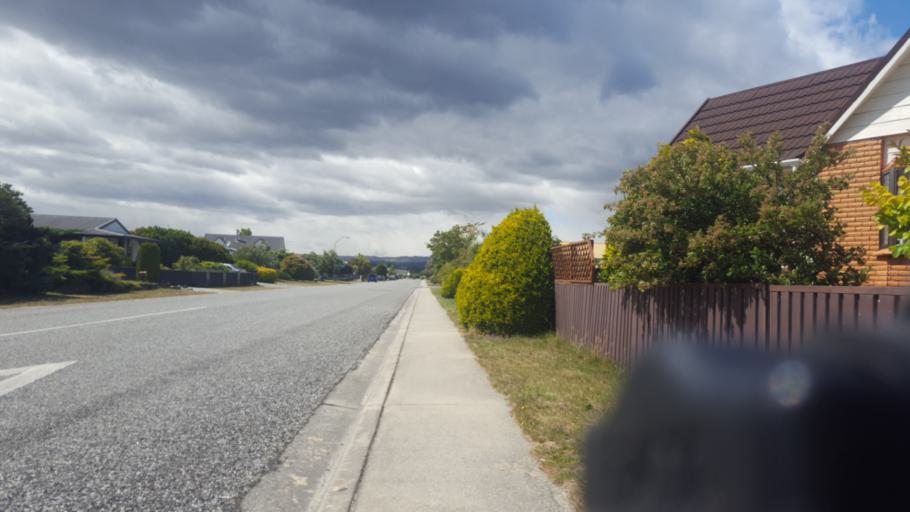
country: NZ
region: Otago
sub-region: Queenstown-Lakes District
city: Wanaka
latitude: -45.1932
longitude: 169.3288
